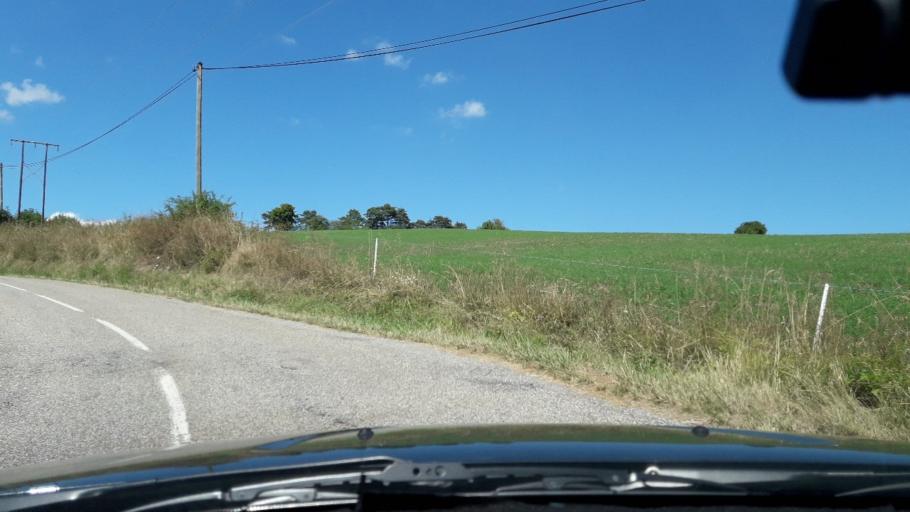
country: FR
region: Rhone-Alpes
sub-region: Departement de l'Isere
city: Mens
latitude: 44.8476
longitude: 5.6247
